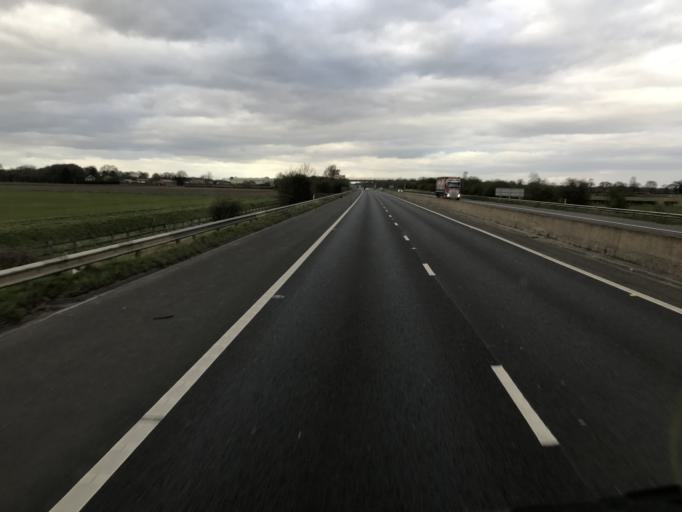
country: GB
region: England
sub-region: Doncaster
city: Hatfield
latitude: 53.5536
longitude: -1.0081
